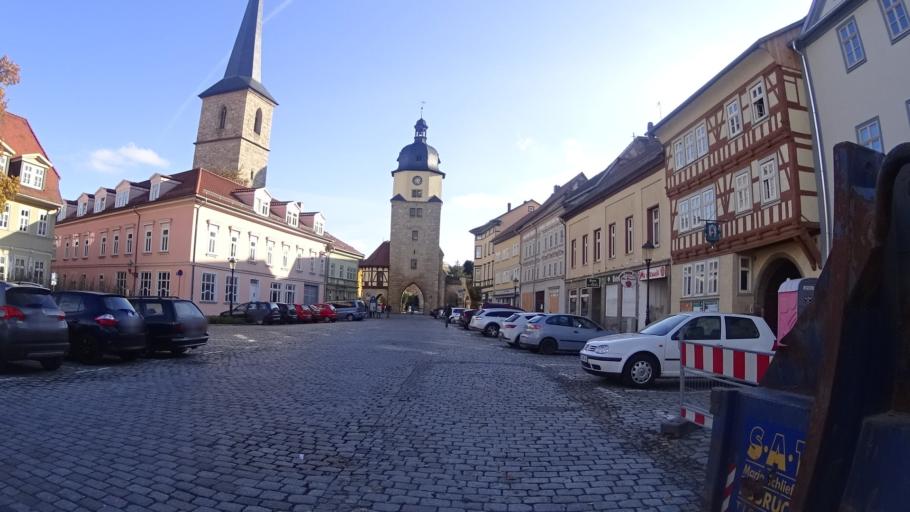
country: DE
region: Thuringia
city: Arnstadt
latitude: 50.8317
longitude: 10.9476
